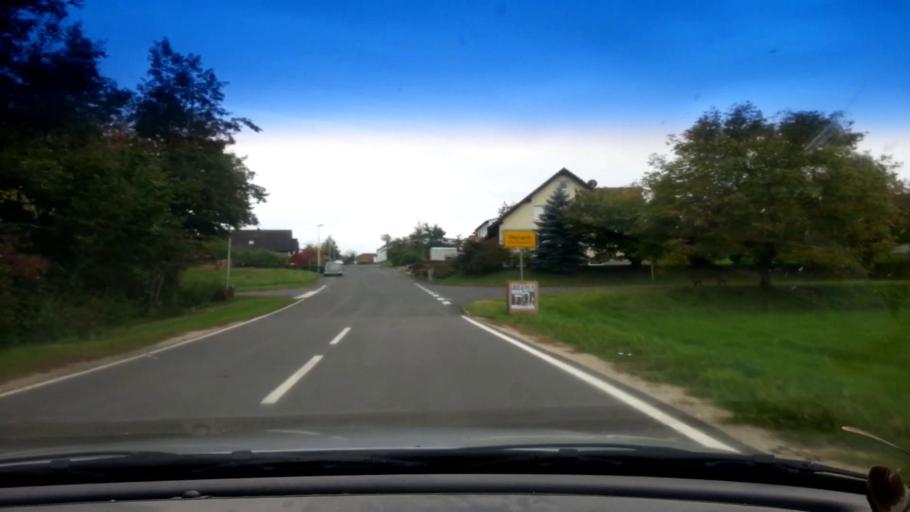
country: DE
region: Bavaria
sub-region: Upper Franconia
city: Gerach
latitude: 50.0330
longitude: 10.8106
